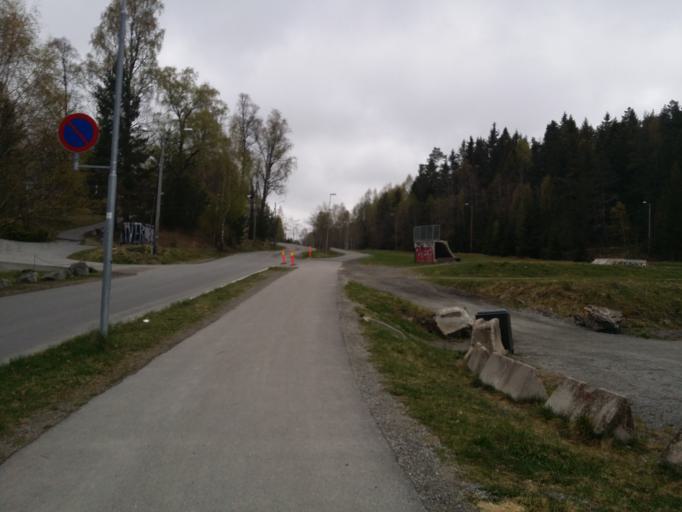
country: NO
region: Akershus
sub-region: Oppegard
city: Kolbotn
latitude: 59.7752
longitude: 10.8150
